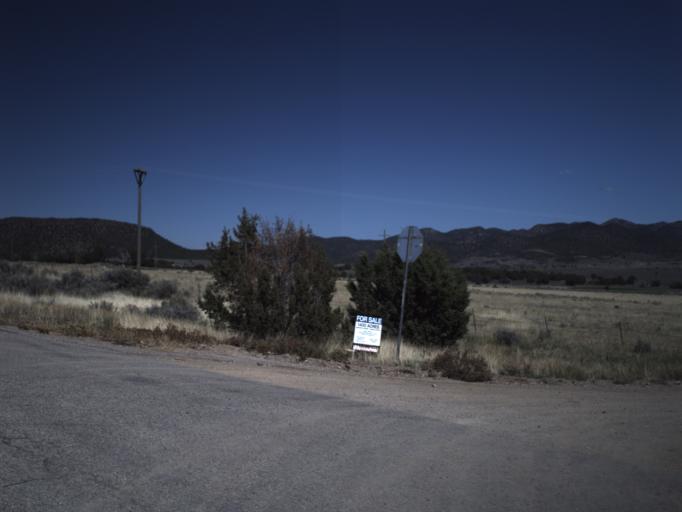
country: US
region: Utah
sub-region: Washington County
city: Enterprise
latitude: 37.5113
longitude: -113.6335
